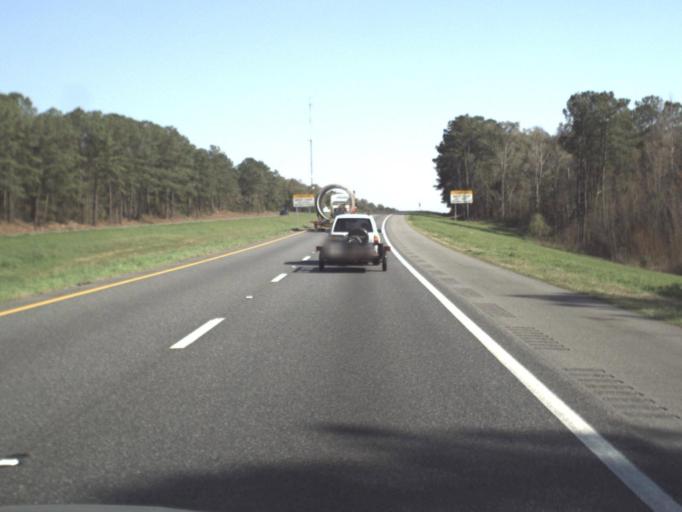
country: US
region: Florida
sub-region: Gadsden County
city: Midway
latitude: 30.5080
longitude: -84.4657
